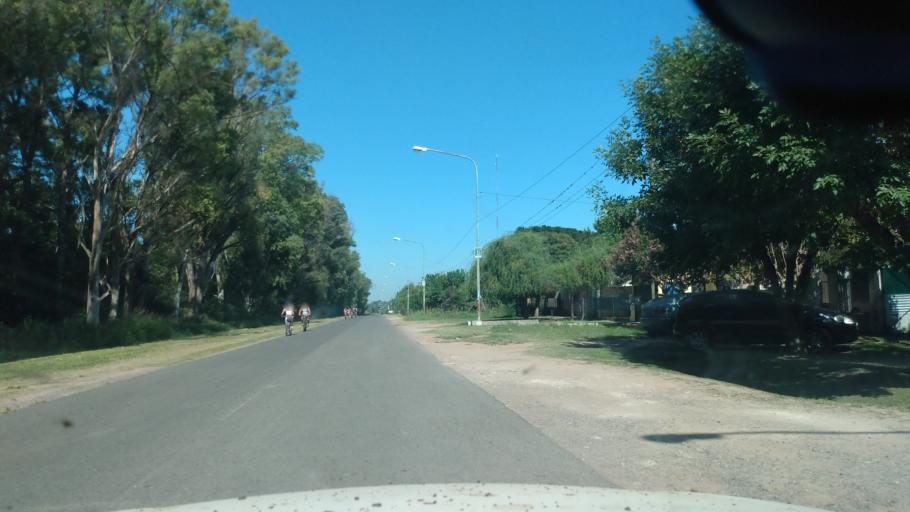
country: AR
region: Buenos Aires
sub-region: Partido de Lujan
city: Lujan
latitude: -34.5042
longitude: -59.0756
